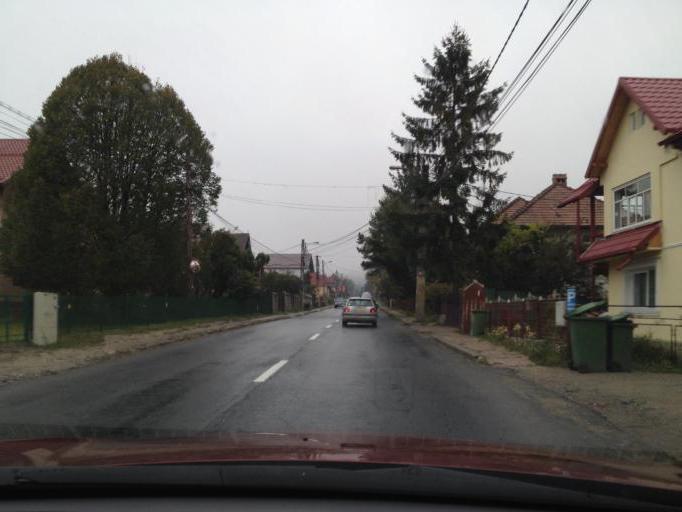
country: RO
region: Brasov
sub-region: Comuna Bran
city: Bran
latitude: 45.5250
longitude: 25.3712
